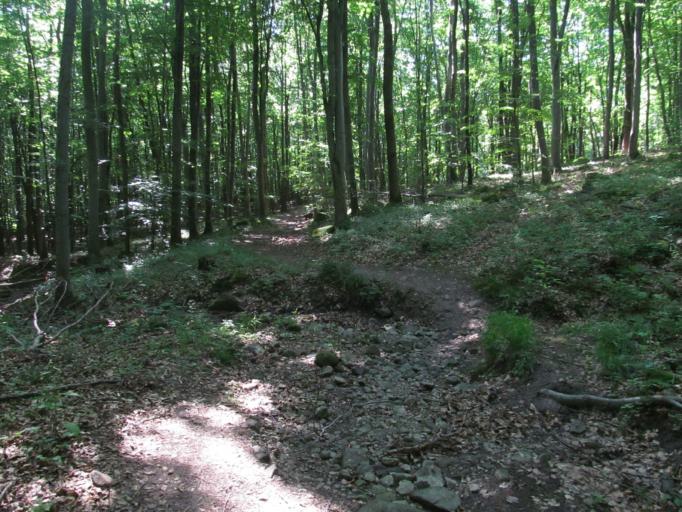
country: HU
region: Pest
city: Pilisszentkereszt
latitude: 47.7160
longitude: 18.9345
